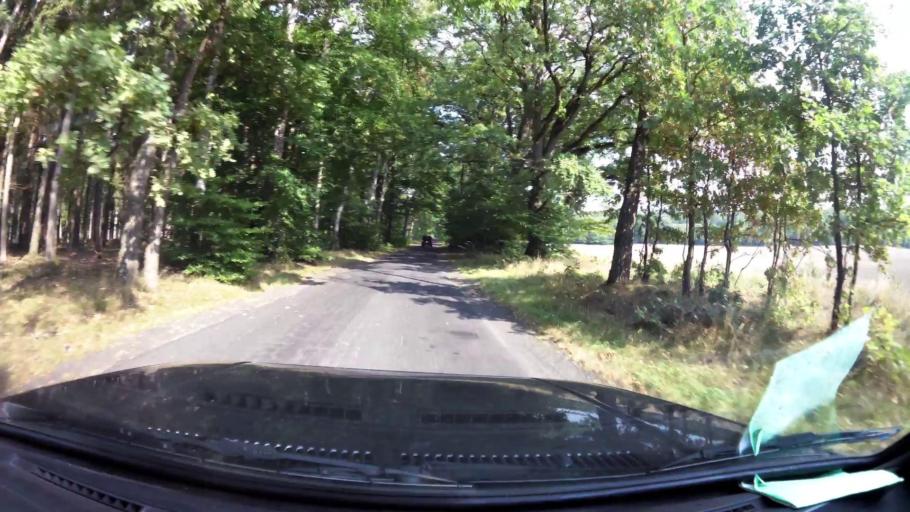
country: PL
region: West Pomeranian Voivodeship
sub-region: Powiat koszalinski
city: Bobolice
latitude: 54.0956
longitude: 16.4886
